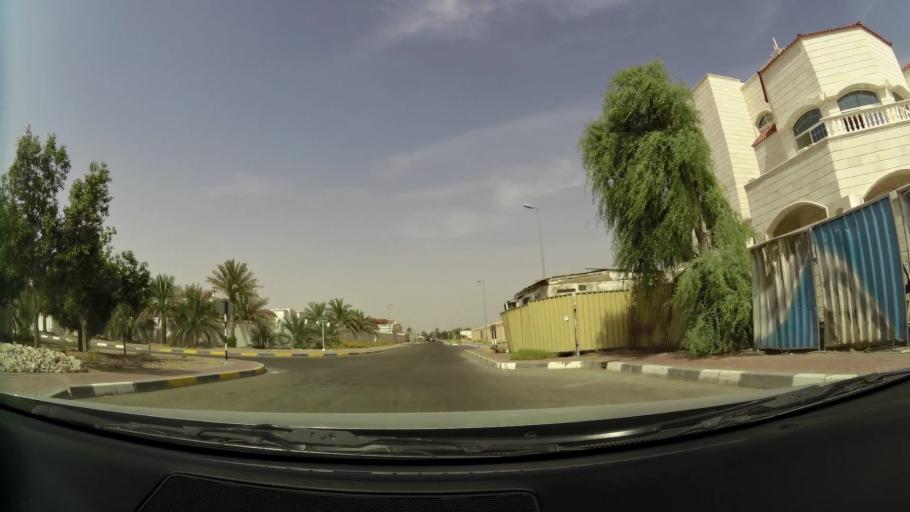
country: AE
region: Abu Dhabi
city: Al Ain
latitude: 24.1592
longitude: 55.6768
